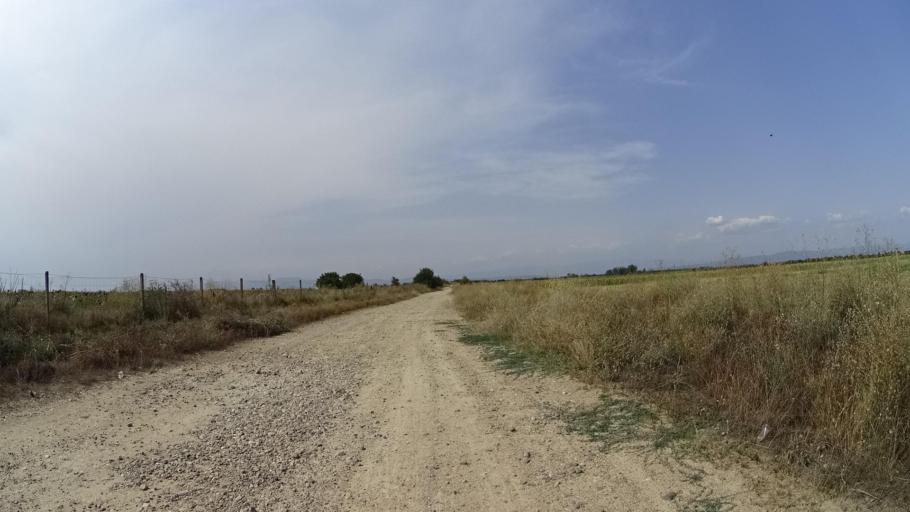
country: BG
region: Plovdiv
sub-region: Obshtina Kaloyanovo
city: Kaloyanovo
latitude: 42.2866
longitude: 24.7974
